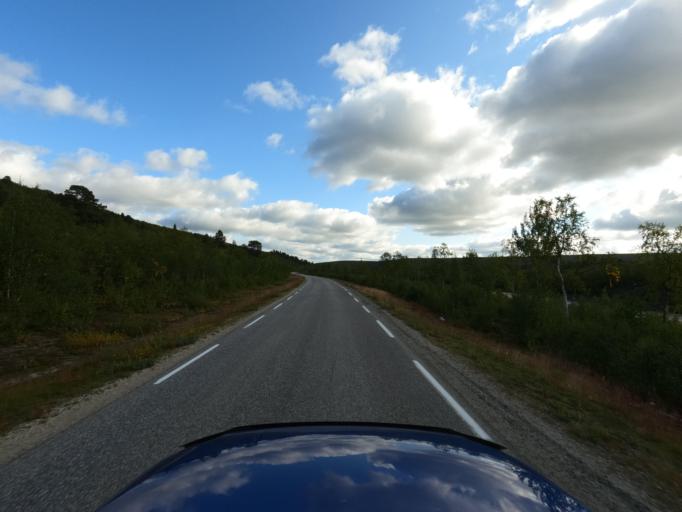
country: NO
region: Finnmark Fylke
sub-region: Porsanger
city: Lakselv
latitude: 69.4242
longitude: 24.8303
